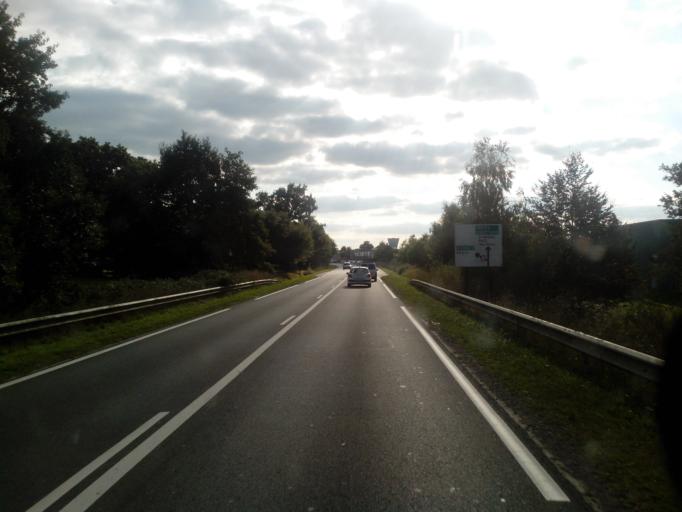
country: FR
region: Brittany
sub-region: Departement d'Ille-et-Vilaine
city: Pace
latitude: 48.1447
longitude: -1.7635
